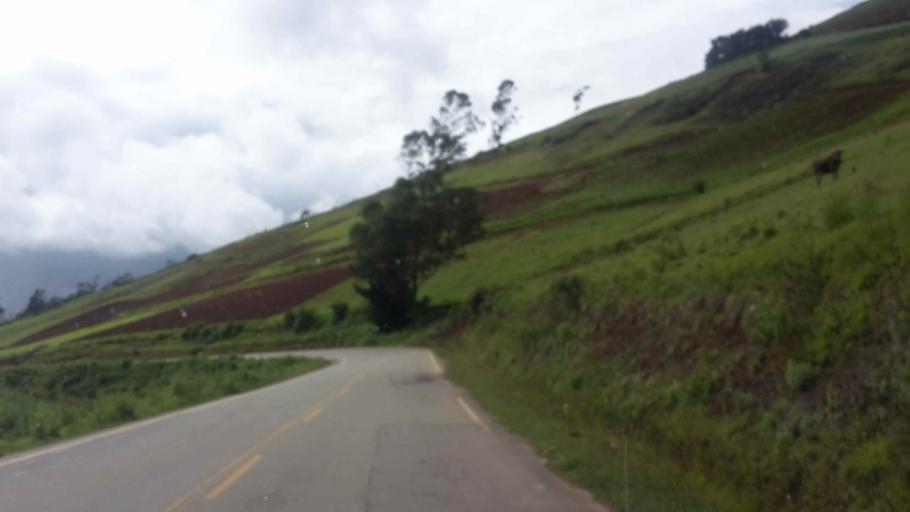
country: BO
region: Cochabamba
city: Totora
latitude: -17.5487
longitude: -65.3551
